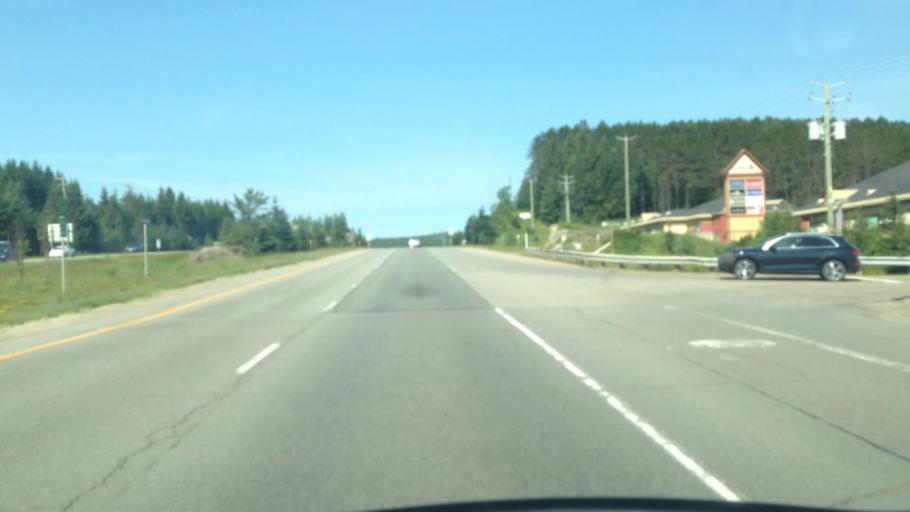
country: CA
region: Quebec
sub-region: Laurentides
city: Mont-Tremblant
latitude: 46.1155
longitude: -74.5811
